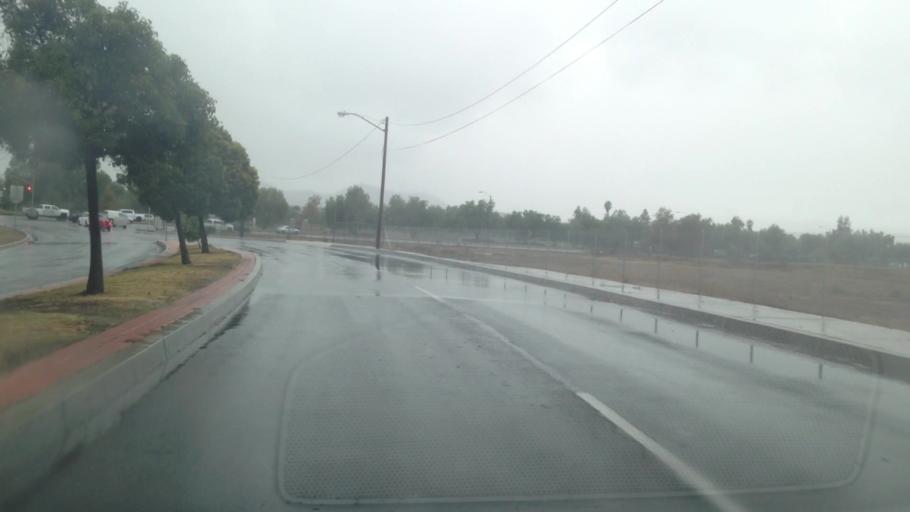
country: US
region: California
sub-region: Riverside County
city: Pedley
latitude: 33.9563
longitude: -117.4556
